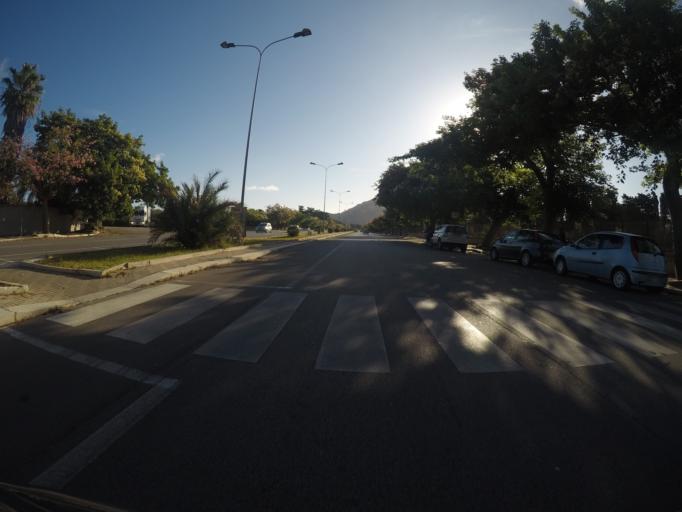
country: IT
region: Sicily
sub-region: Palermo
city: Isola delle Femmine
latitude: 38.1889
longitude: 13.3080
